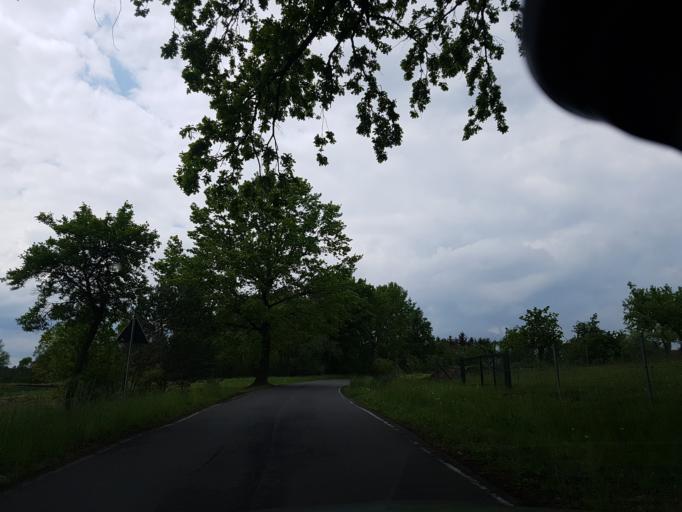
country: DE
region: Brandenburg
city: Crinitz
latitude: 51.7611
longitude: 13.7497
